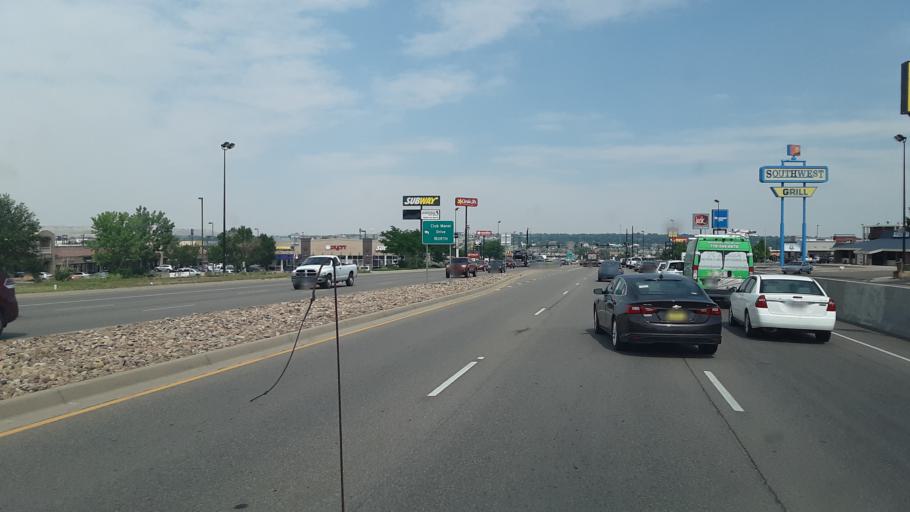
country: US
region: Colorado
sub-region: Pueblo County
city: Pueblo
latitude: 38.3084
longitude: -104.6232
